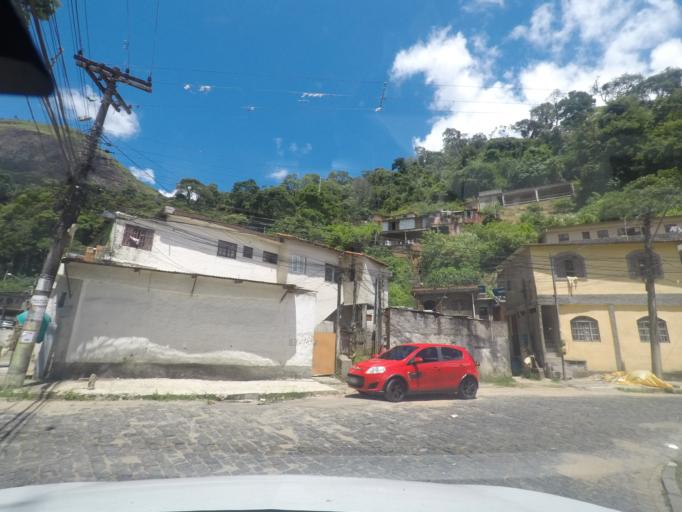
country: BR
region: Rio de Janeiro
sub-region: Teresopolis
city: Teresopolis
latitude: -22.4228
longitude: -42.9871
